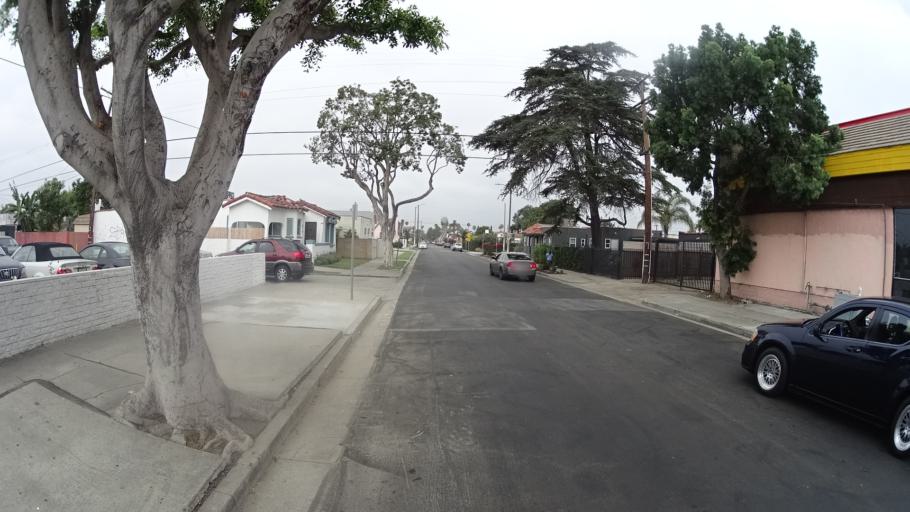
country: US
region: California
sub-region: Los Angeles County
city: View Park-Windsor Hills
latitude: 34.0294
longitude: -118.3357
